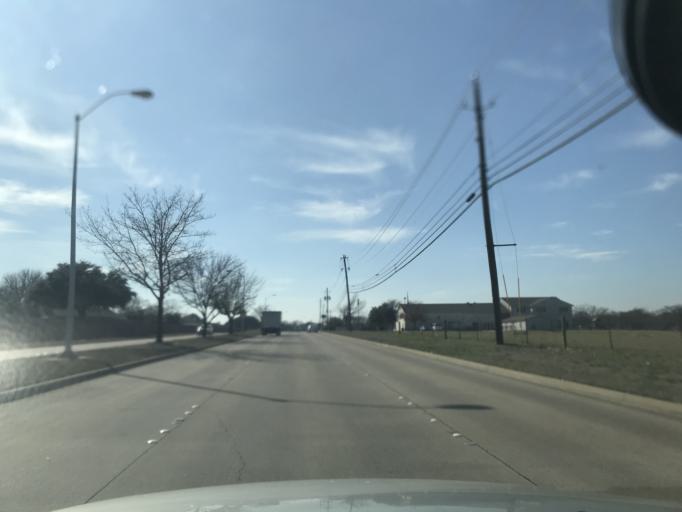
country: US
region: Texas
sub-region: Collin County
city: Plano
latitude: 33.0430
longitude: -96.6855
